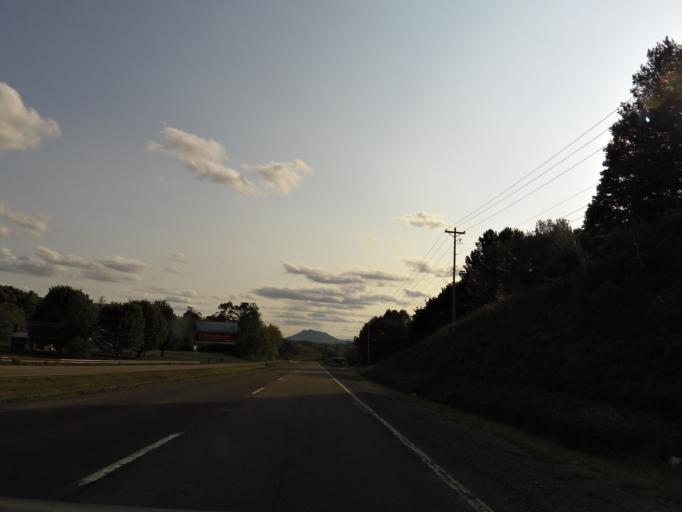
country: US
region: Virginia
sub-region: Tazewell County
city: Springville
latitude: 37.1653
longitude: -81.4588
